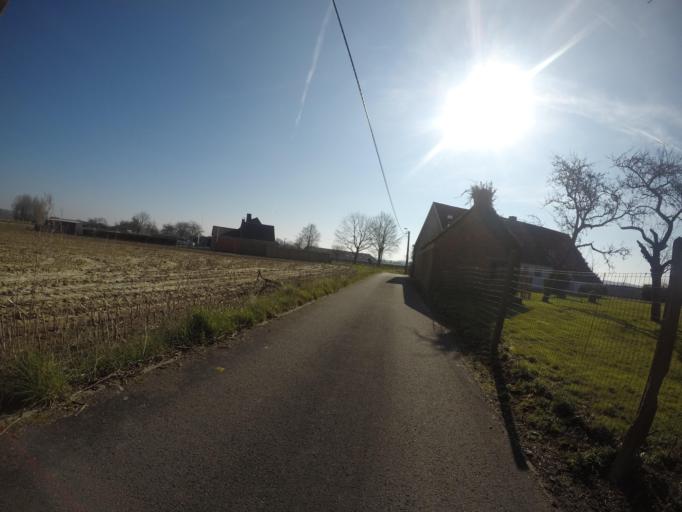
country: BE
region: Flanders
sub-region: Provincie Oost-Vlaanderen
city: Sint-Maria-Lierde
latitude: 50.8015
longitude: 3.7922
